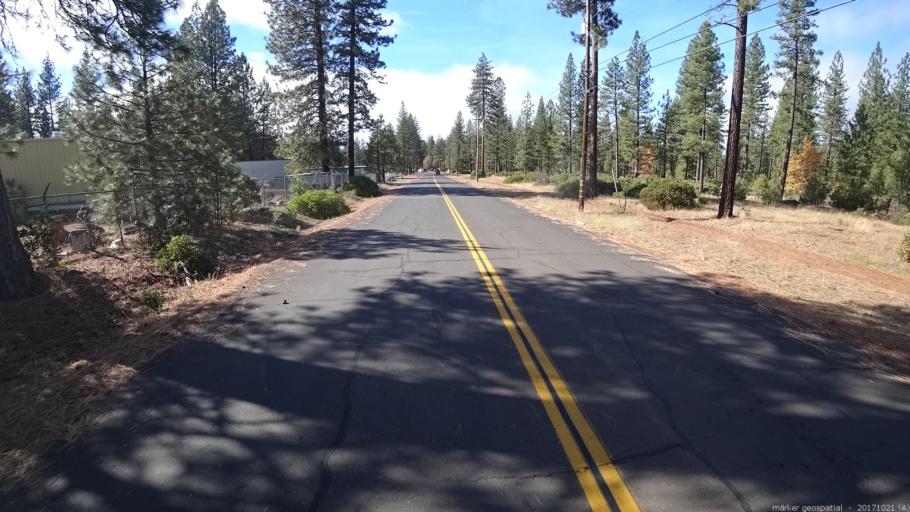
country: US
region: California
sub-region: Shasta County
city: Burney
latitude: 40.8849
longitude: -121.6486
